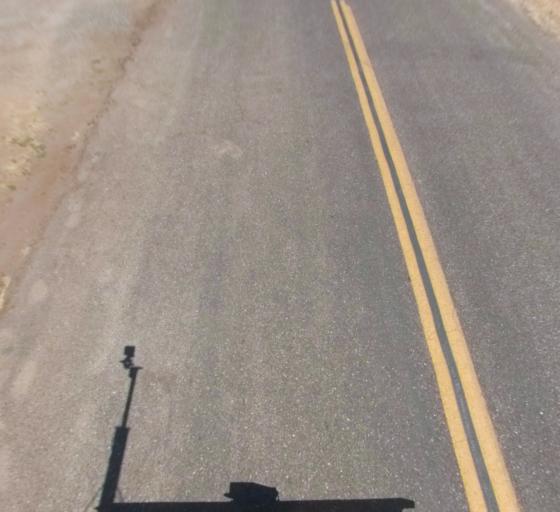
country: US
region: California
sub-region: Madera County
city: Parksdale
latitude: 36.9100
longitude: -119.9576
